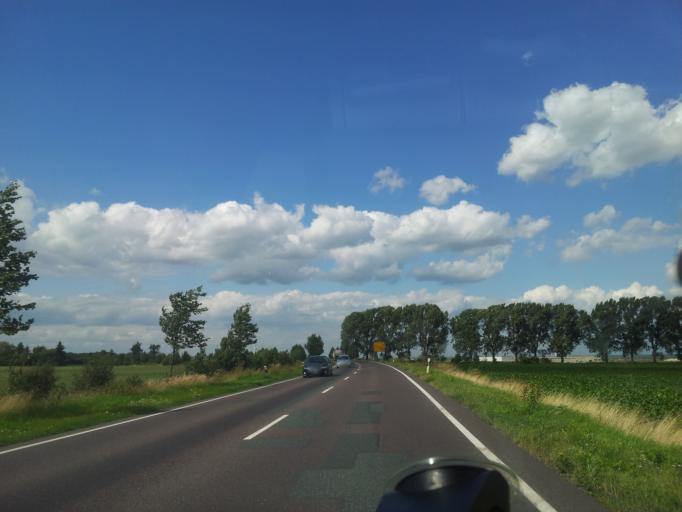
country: DE
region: Saxony-Anhalt
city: Meitzendorf
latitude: 52.2193
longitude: 11.5401
